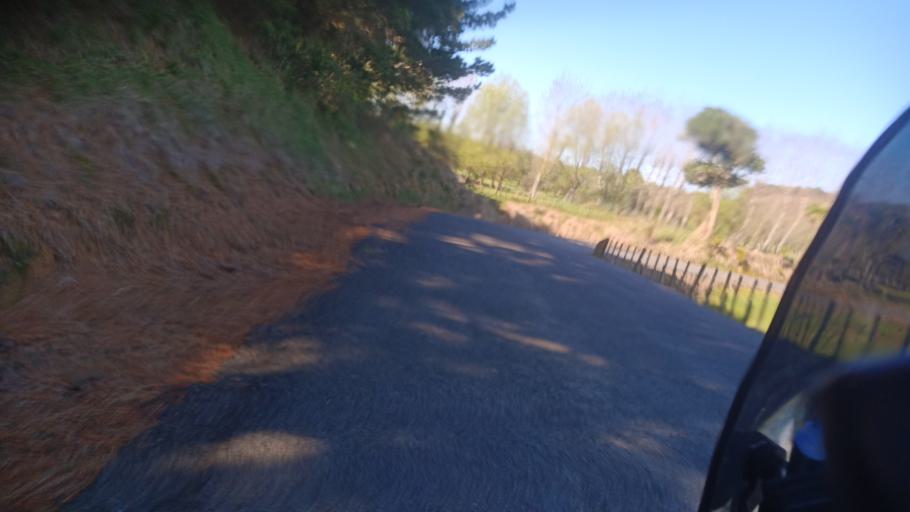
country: NZ
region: Gisborne
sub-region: Gisborne District
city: Gisborne
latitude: -39.1480
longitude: 177.9236
